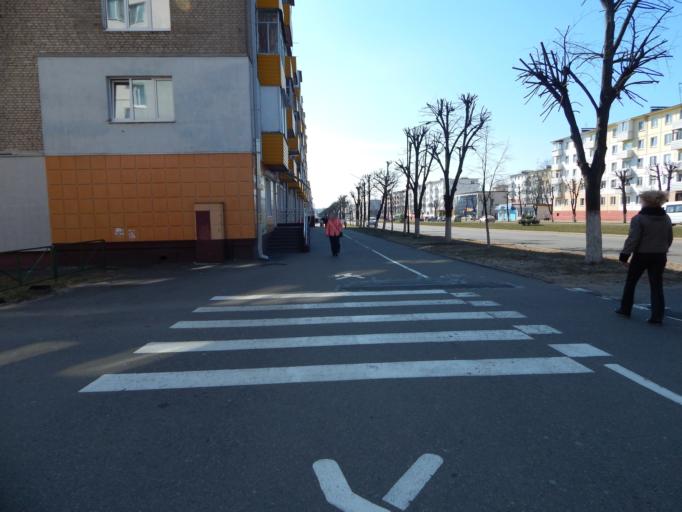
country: BY
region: Minsk
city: Horad Barysaw
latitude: 54.2188
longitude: 28.5087
